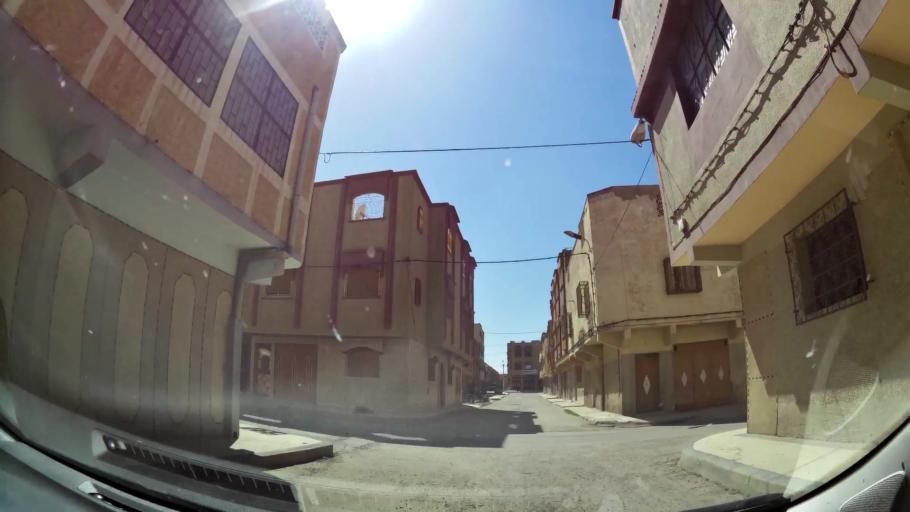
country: MA
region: Oriental
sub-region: Oujda-Angad
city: Oujda
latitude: 34.6832
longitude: -1.9375
